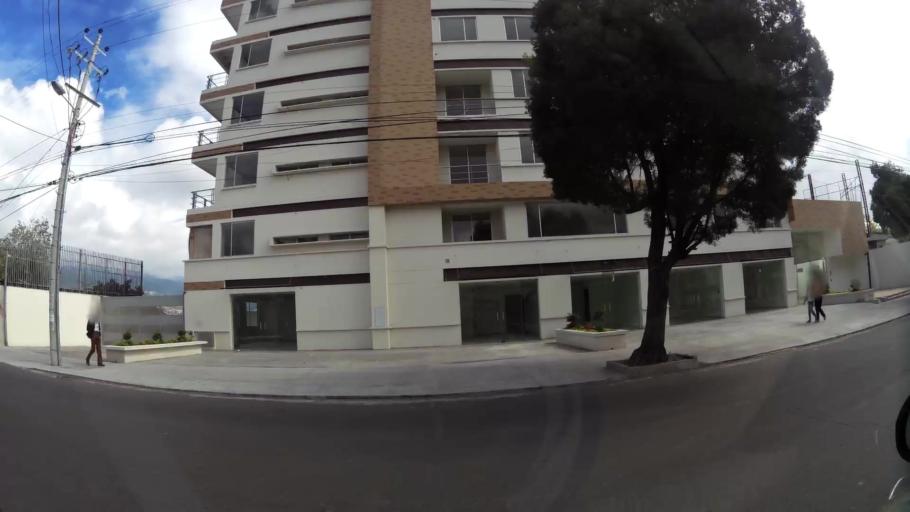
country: EC
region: Pichincha
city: Quito
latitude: -0.1566
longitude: -78.4710
